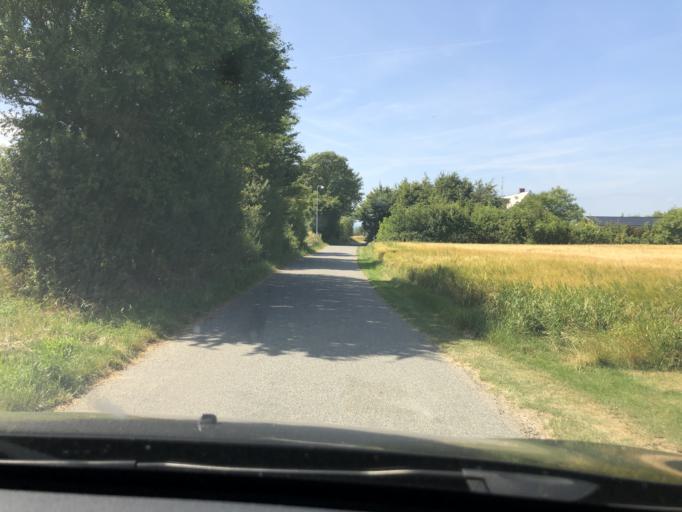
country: DK
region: South Denmark
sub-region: AEro Kommune
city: AEroskobing
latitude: 54.8950
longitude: 10.2913
